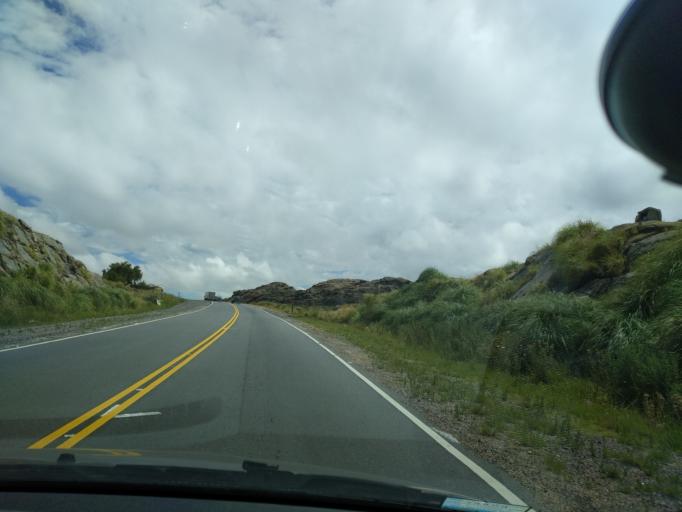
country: AR
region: Cordoba
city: Mina Clavero
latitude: -31.6983
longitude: -64.8945
